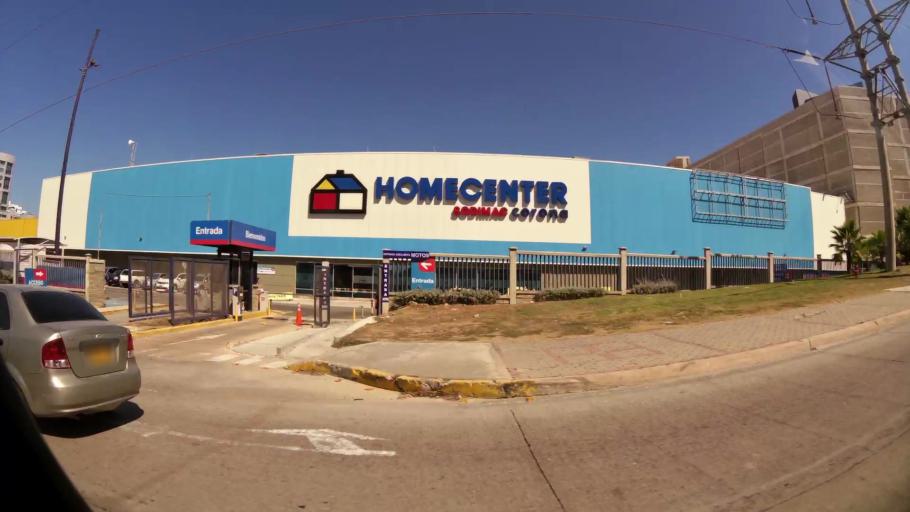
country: CO
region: Atlantico
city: Barranquilla
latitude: 11.0155
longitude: -74.8296
